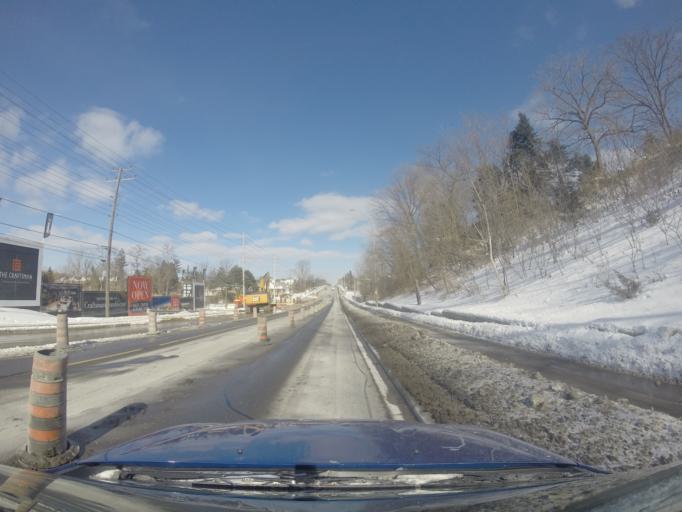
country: CA
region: Ontario
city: Mississauga
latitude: 43.5205
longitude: -79.6195
